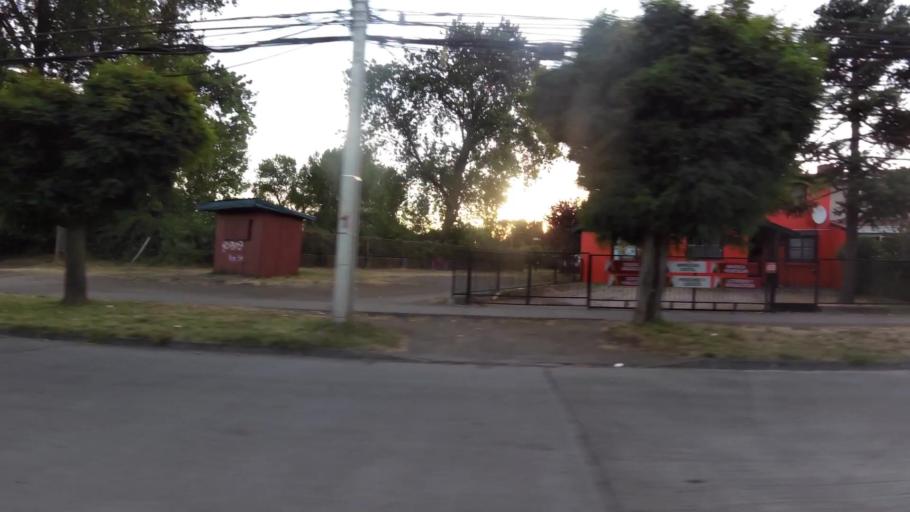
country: CL
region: Biobio
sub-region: Provincia de Concepcion
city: Concepcion
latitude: -36.8431
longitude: -73.0989
